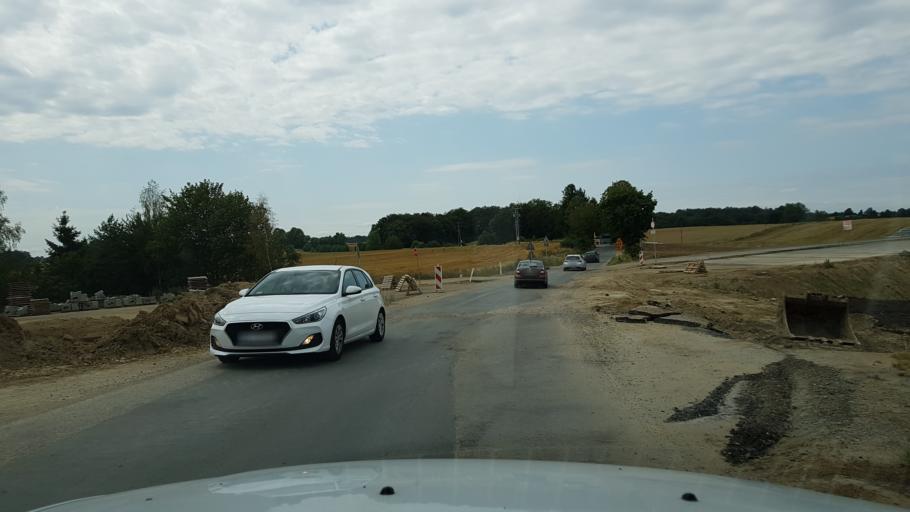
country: PL
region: West Pomeranian Voivodeship
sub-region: Powiat koszalinski
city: Mielno
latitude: 54.1980
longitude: 16.0125
